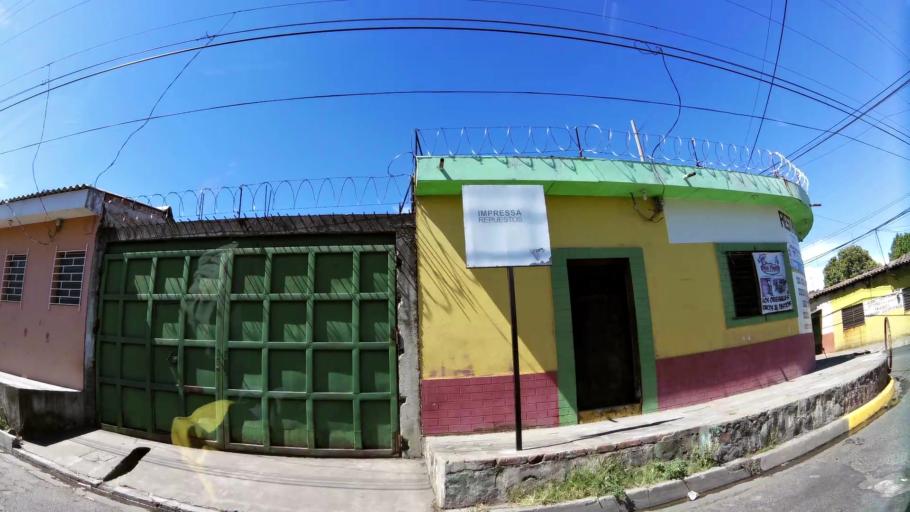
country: SV
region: La Libertad
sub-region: Distrito de Quezaltepeque
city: Quezaltepeque
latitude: 13.8317
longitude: -89.2751
